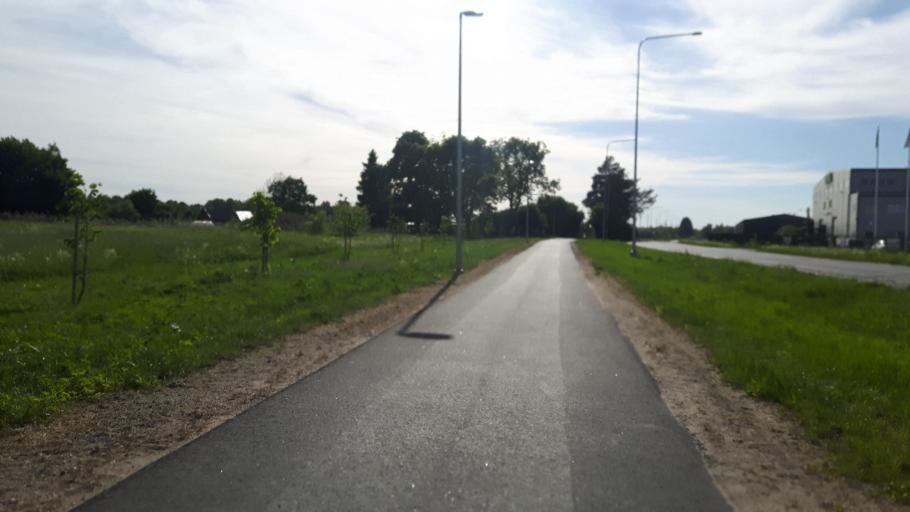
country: EE
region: Harju
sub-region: Joelaehtme vald
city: Loo
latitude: 59.4305
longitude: 24.9706
